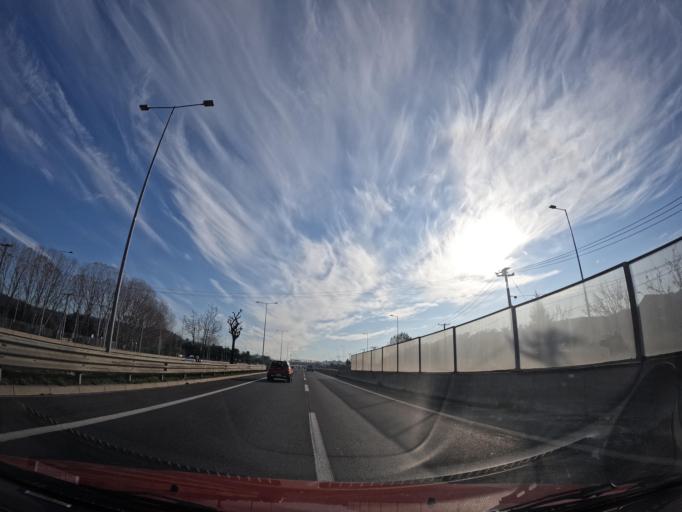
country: CL
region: Biobio
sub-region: Provincia de Concepcion
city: Concepcion
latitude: -36.8189
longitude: -73.0073
